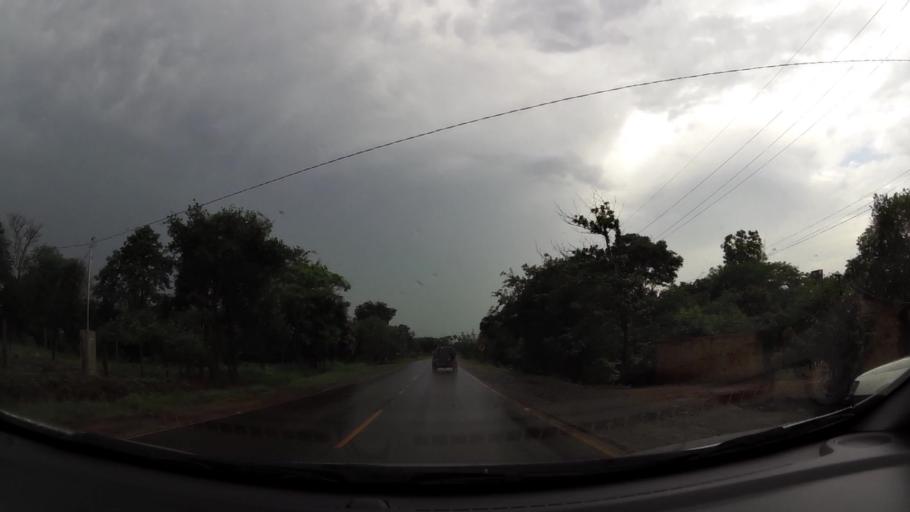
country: PY
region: Alto Parana
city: Presidente Franco
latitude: -25.5760
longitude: -54.6692
